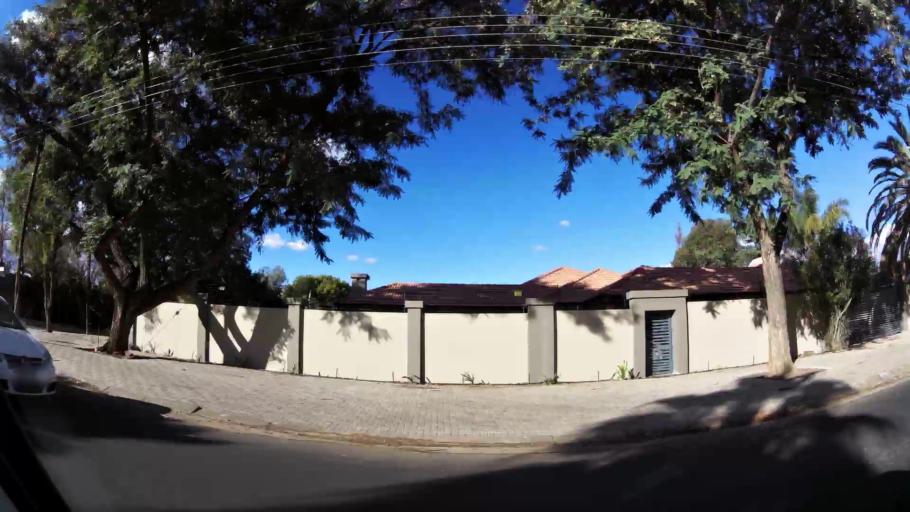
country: ZA
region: Limpopo
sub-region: Capricorn District Municipality
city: Polokwane
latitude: -23.9289
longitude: 29.4525
